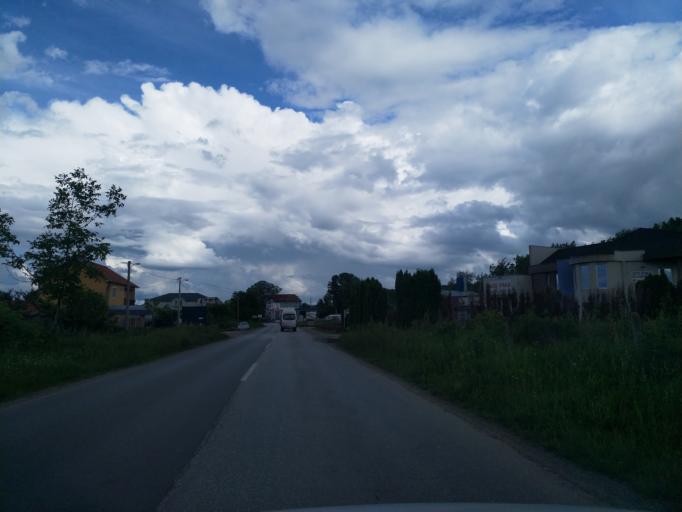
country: RS
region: Central Serbia
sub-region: Pomoravski Okrug
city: Cuprija
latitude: 43.9398
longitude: 21.3630
